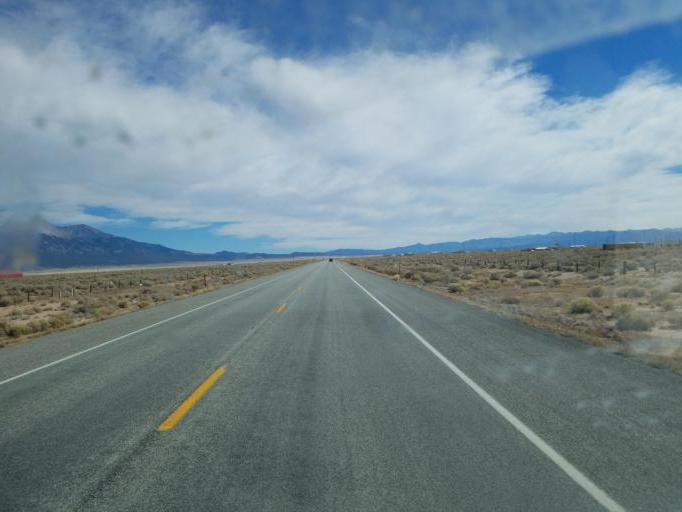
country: US
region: Colorado
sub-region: Alamosa County
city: Alamosa East
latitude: 37.4749
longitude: -105.7055
